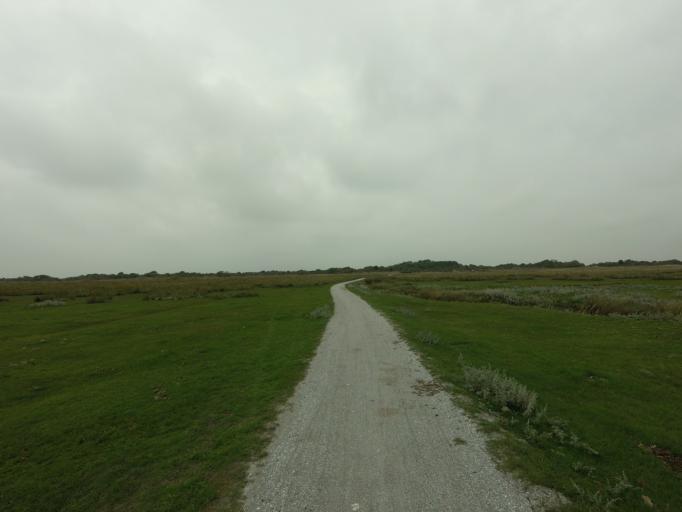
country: NL
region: Friesland
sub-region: Gemeente Schiermonnikoog
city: Schiermonnikoog
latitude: 53.4849
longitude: 6.2171
